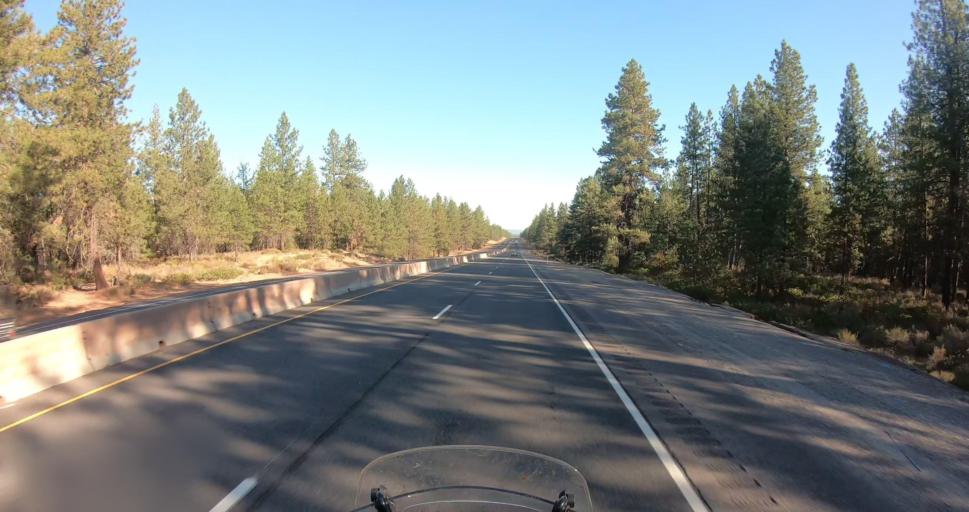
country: US
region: Oregon
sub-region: Deschutes County
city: Deschutes River Woods
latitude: 43.9318
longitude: -121.3522
